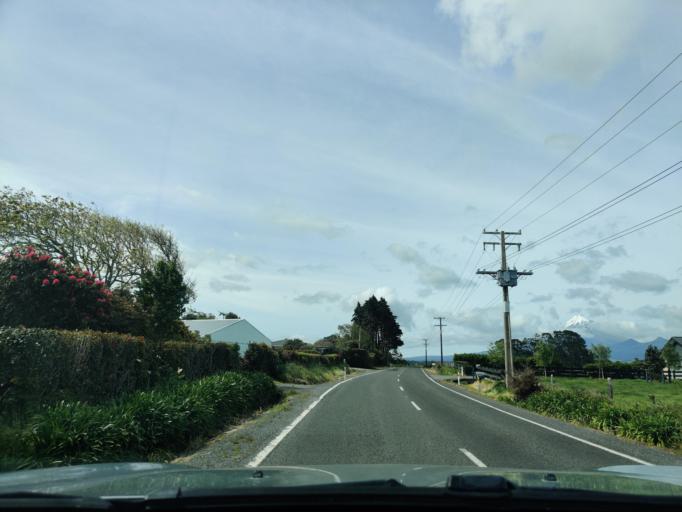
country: NZ
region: Taranaki
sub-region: New Plymouth District
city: New Plymouth
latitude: -39.1070
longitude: 174.0999
